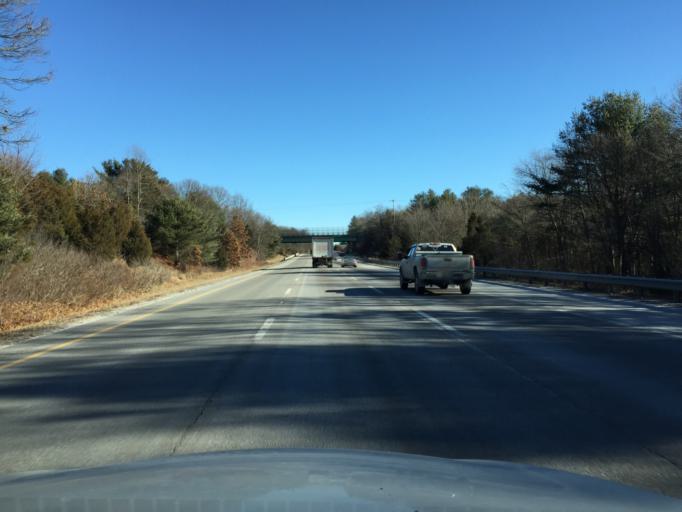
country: US
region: Massachusetts
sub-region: Norfolk County
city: Foxborough
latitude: 42.0315
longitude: -71.2764
